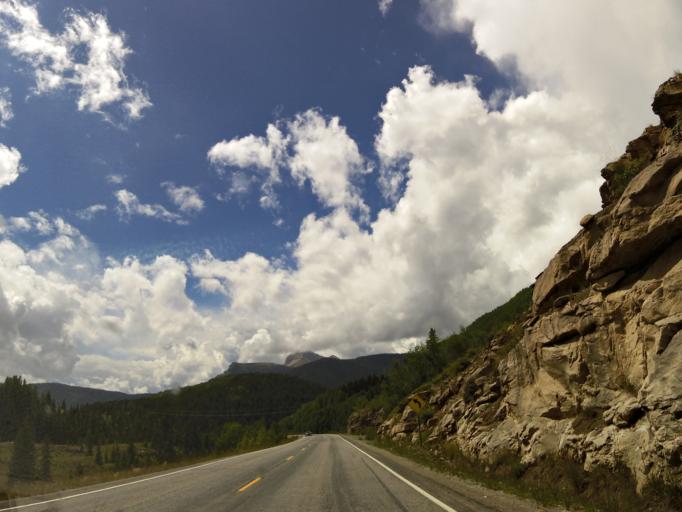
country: US
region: Colorado
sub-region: San Juan County
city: Silverton
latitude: 37.7289
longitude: -107.7303
